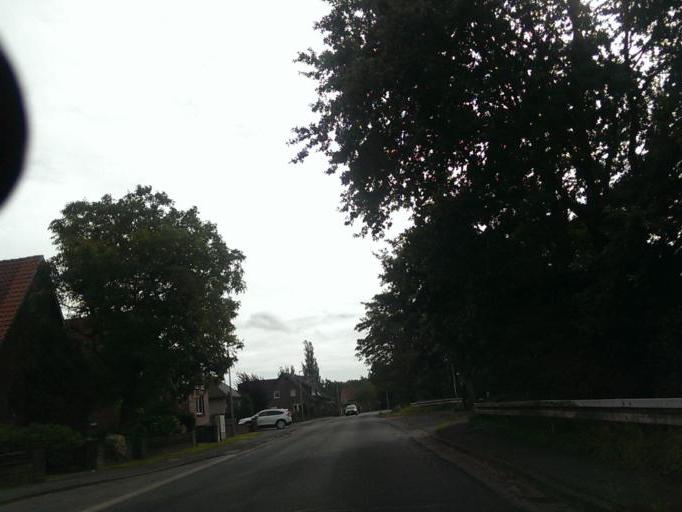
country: DE
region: Lower Saxony
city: Neustadt am Rubenberge
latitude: 52.4581
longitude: 9.4816
